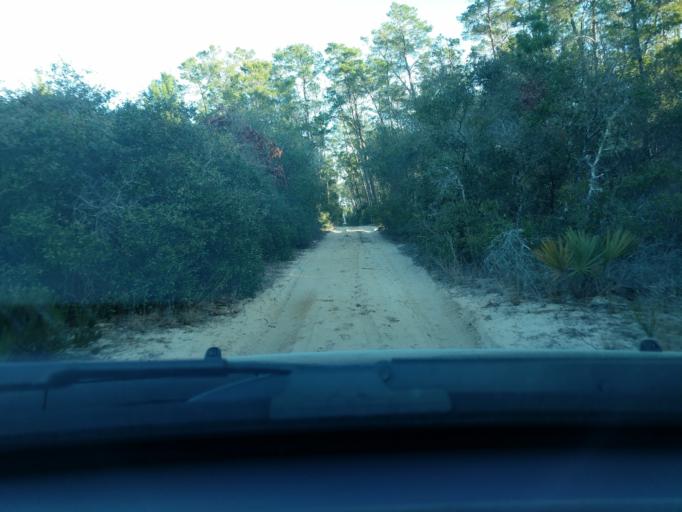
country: US
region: Florida
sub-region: Lake County
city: Astor
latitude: 29.2181
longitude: -81.7409
